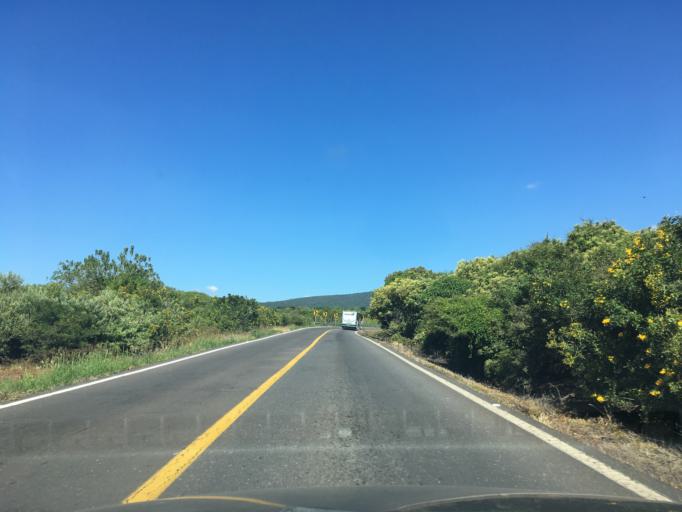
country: MX
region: Mexico
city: Tlazazalca
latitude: 20.0285
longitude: -102.0642
